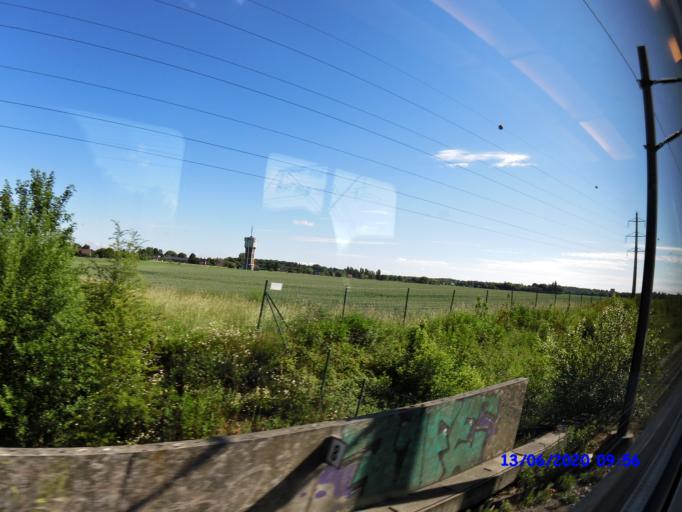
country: BE
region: Wallonia
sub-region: Province de Liege
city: Awans
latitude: 50.6590
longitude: 5.4667
